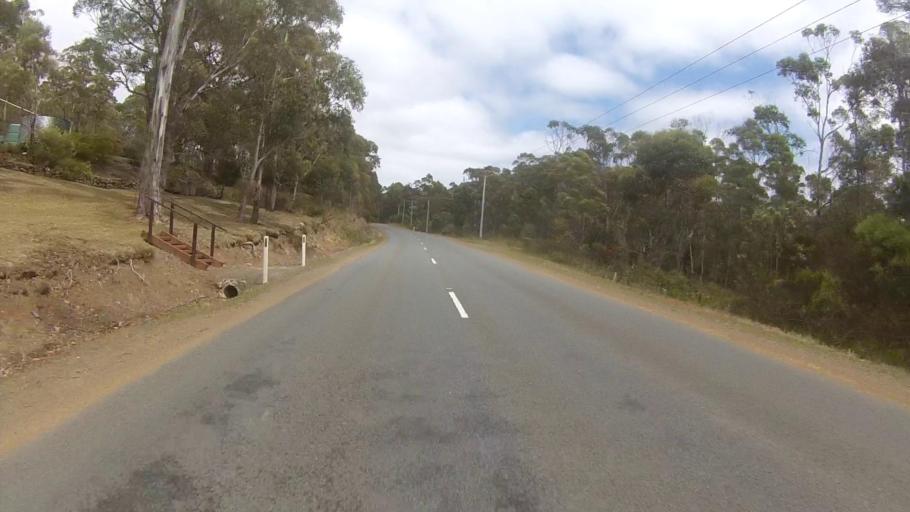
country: AU
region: Tasmania
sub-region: Kingborough
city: Margate
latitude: -42.9925
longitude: 147.2141
